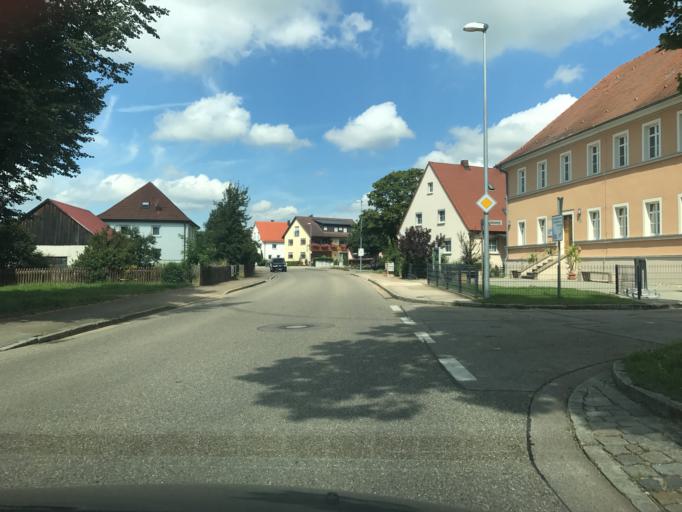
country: DE
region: Bavaria
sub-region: Regierungsbezirk Mittelfranken
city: Gerolfingen
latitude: 49.0530
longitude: 10.5110
